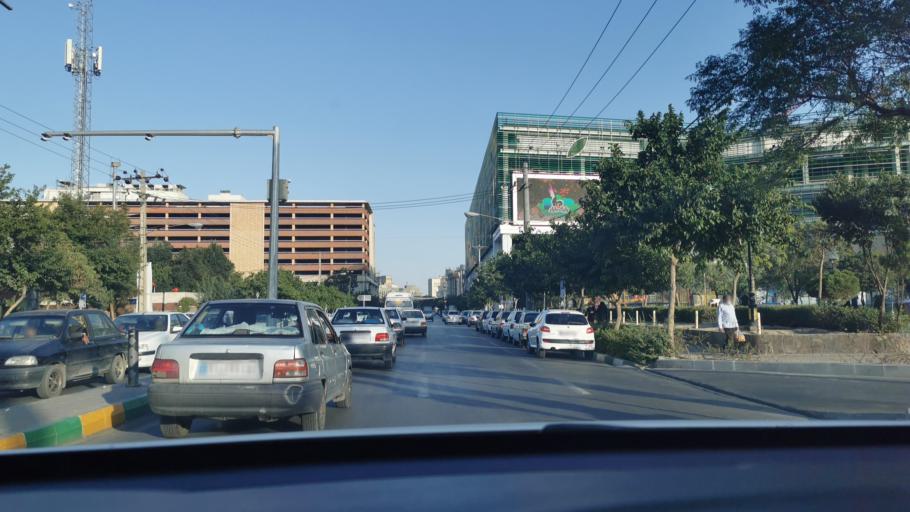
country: IR
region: Razavi Khorasan
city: Mashhad
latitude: 36.2933
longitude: 59.6459
